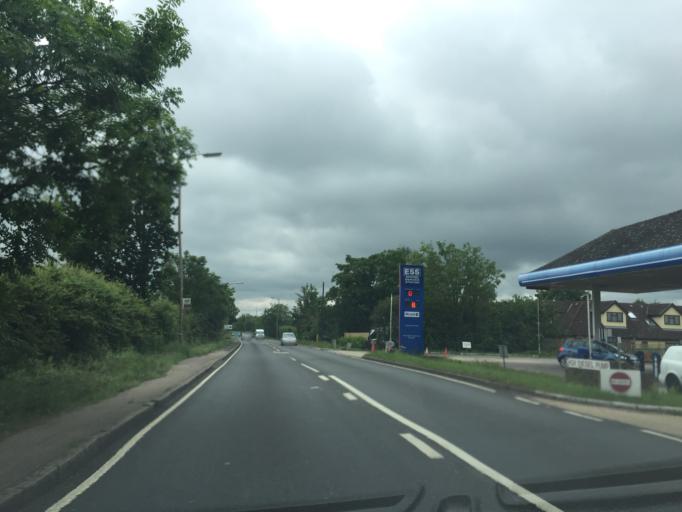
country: GB
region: England
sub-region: Essex
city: Epping
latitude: 51.7303
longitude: 0.1238
